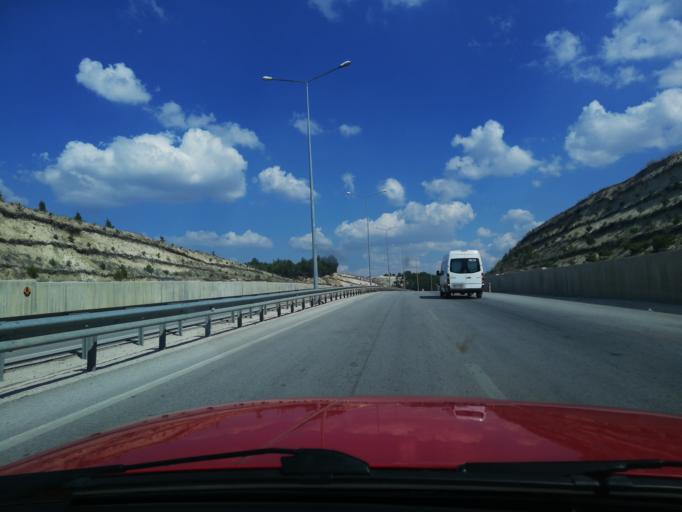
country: TR
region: Burdur
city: Burdur
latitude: 37.7011
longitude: 30.3142
